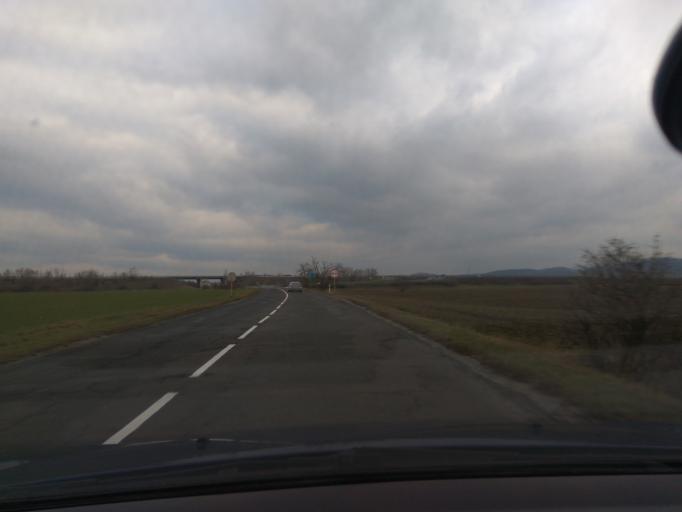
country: SK
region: Trnavsky
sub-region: Okres Trnava
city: Piestany
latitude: 48.6448
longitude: 17.8382
